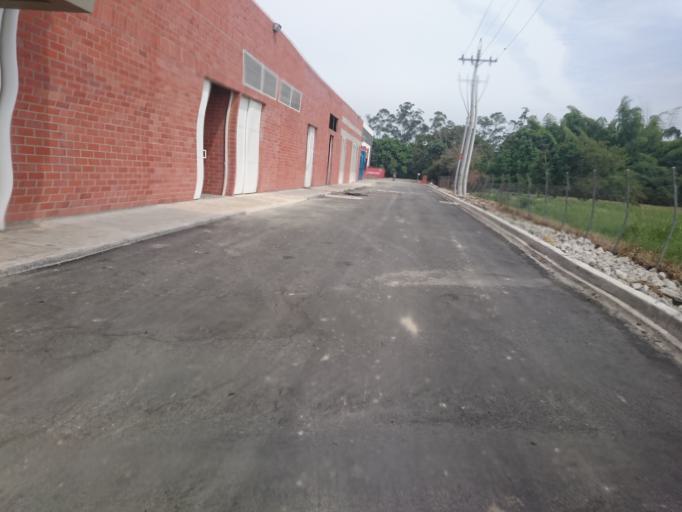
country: CO
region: Cauca
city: Puerto Tejada
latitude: 3.2106
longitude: -76.4265
